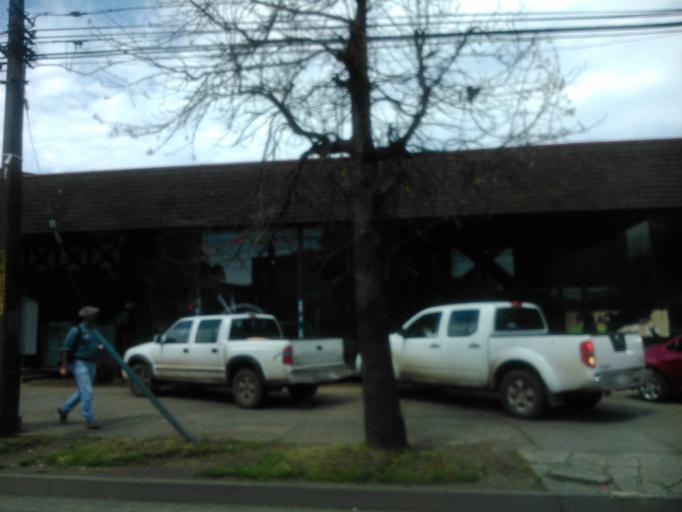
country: CL
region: Araucania
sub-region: Provincia de Cautin
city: Temuco
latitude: -38.7401
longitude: -72.6014
